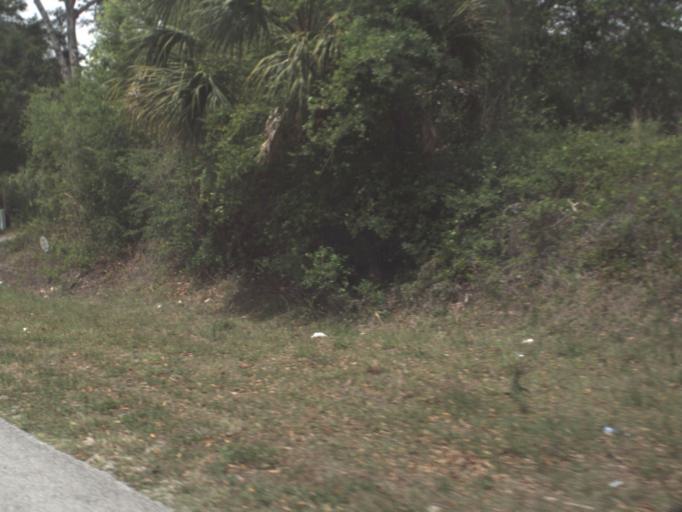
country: US
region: Florida
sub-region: Lake County
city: Mount Plymouth
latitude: 28.8893
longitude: -81.4656
